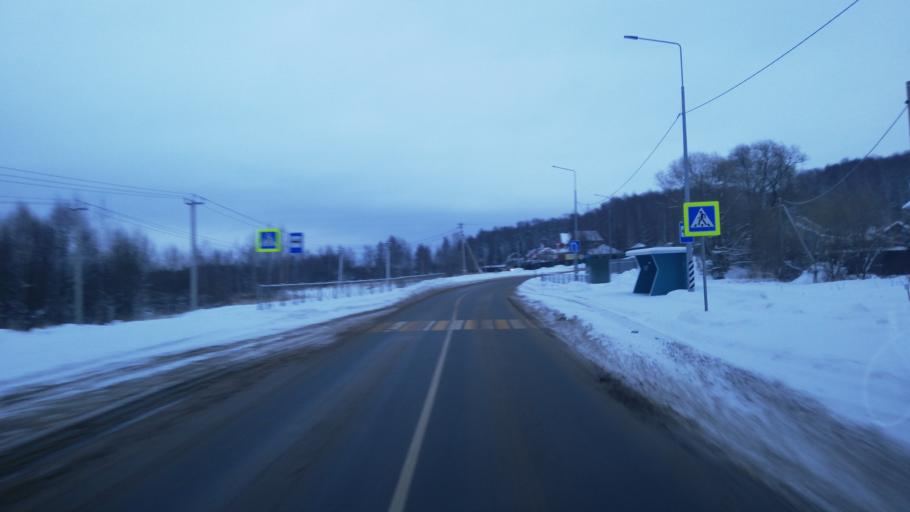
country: RU
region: Jaroslavl
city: Yaroslavl
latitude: 57.4980
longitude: 39.9300
